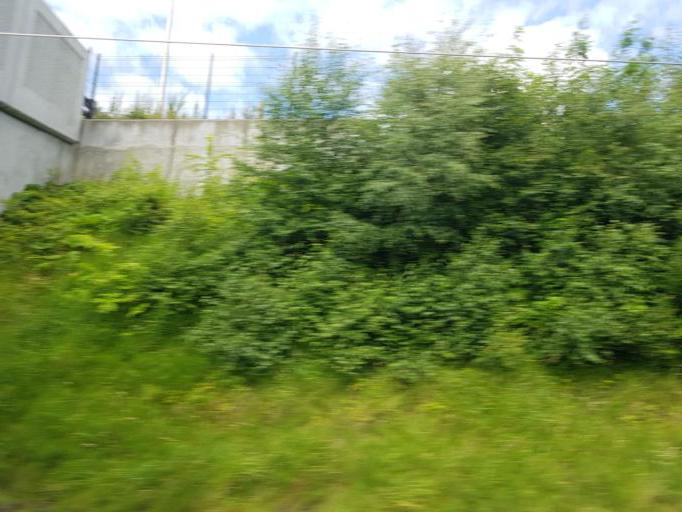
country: GB
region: Scotland
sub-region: North Lanarkshire
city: Kilsyth
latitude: 55.9441
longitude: -4.0717
